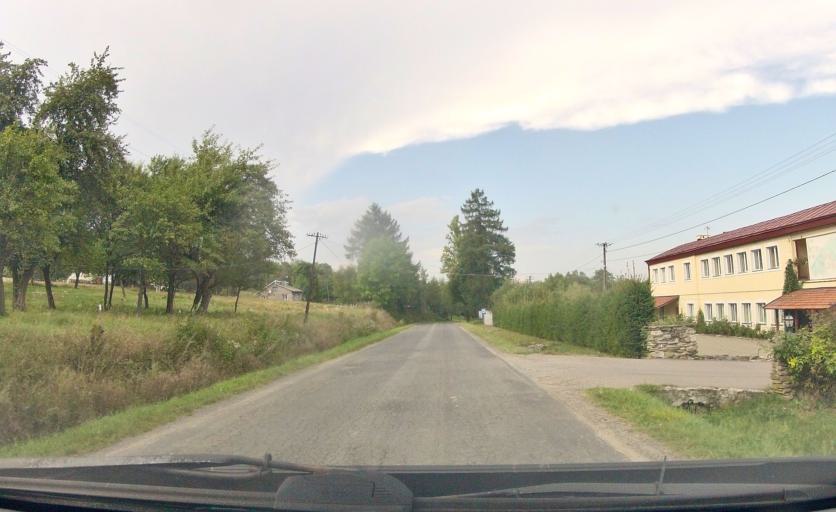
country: PL
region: Subcarpathian Voivodeship
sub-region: Powiat krosnienski
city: Dukla
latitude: 49.5235
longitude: 21.6153
